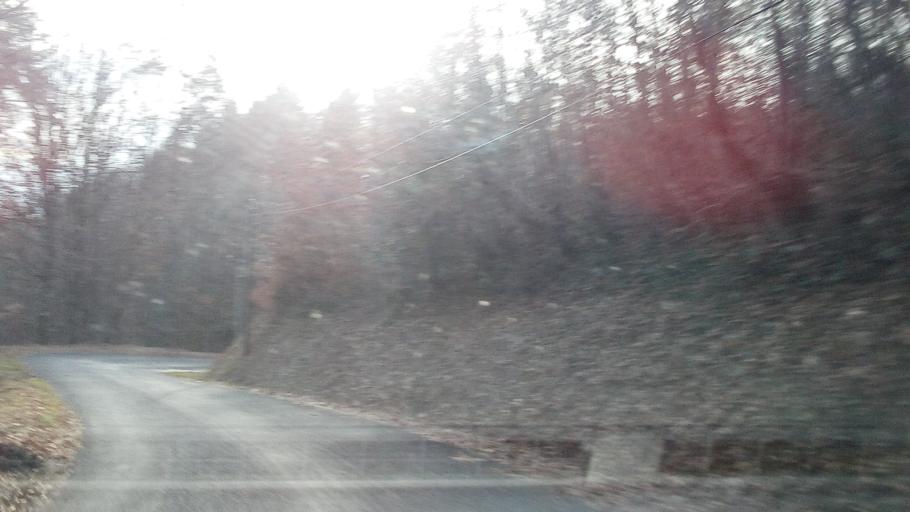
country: FR
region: Limousin
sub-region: Departement de la Correze
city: Naves
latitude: 45.3022
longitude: 1.7830
